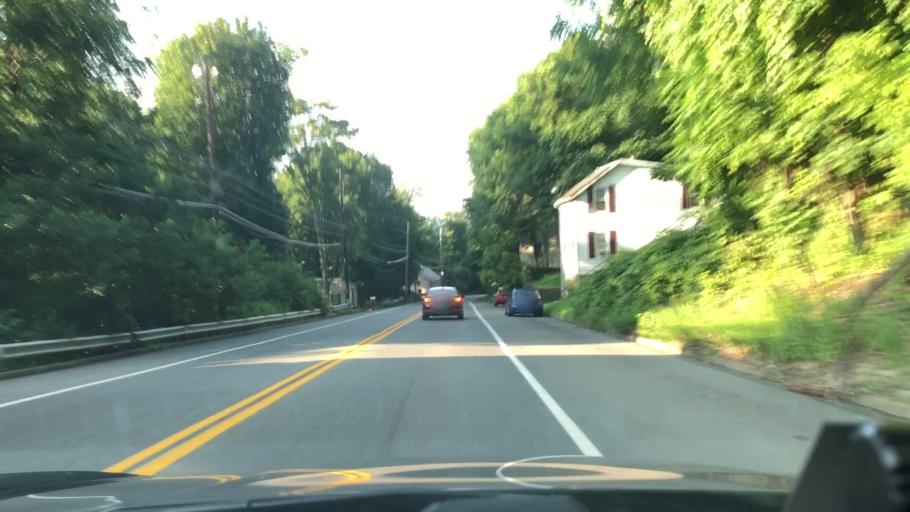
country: US
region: Pennsylvania
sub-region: Lehigh County
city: Fountain Hill
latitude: 40.5999
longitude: -75.3890
